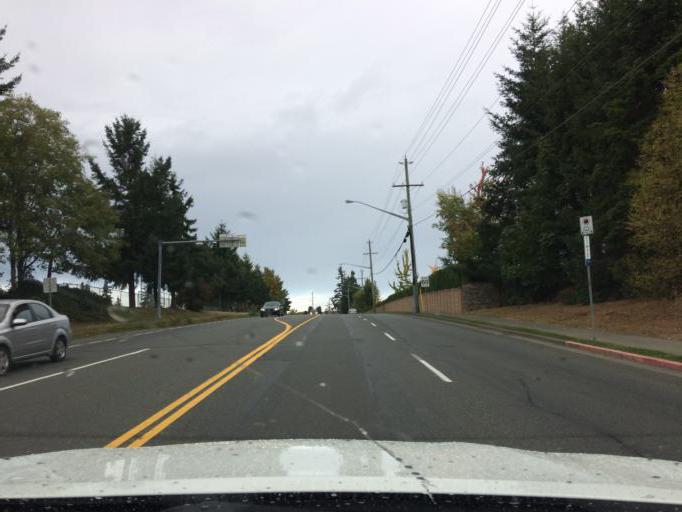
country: CA
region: British Columbia
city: Courtenay
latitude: 49.6993
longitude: -124.9561
